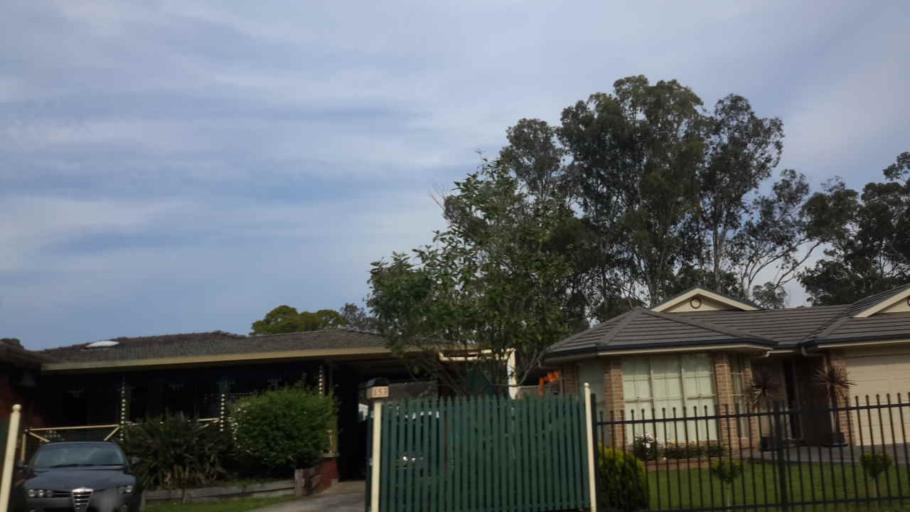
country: AU
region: New South Wales
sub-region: Penrith Municipality
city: Cambridge Park
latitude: -33.7461
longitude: 150.7144
